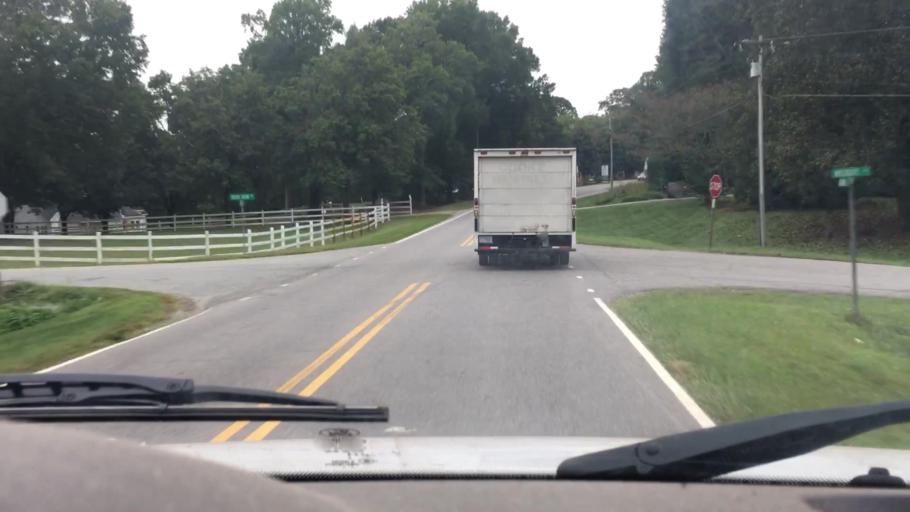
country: US
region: North Carolina
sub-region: Catawba County
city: Lake Norman of Catawba
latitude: 35.5578
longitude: -80.9906
